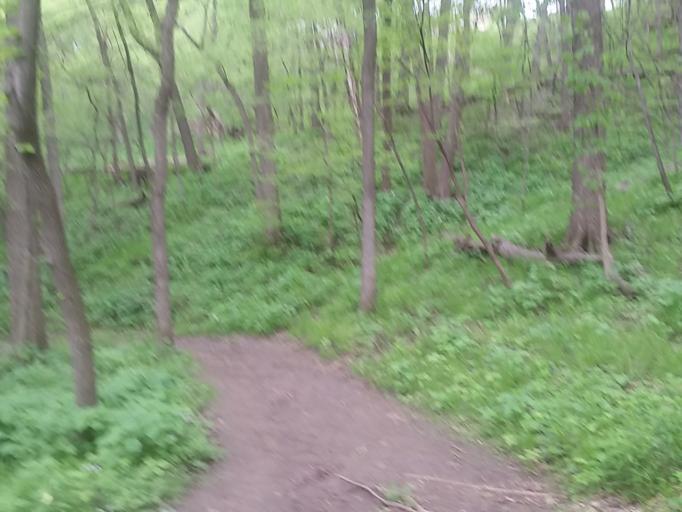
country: US
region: Nebraska
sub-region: Sarpy County
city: Bellevue
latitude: 41.1795
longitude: -95.9169
